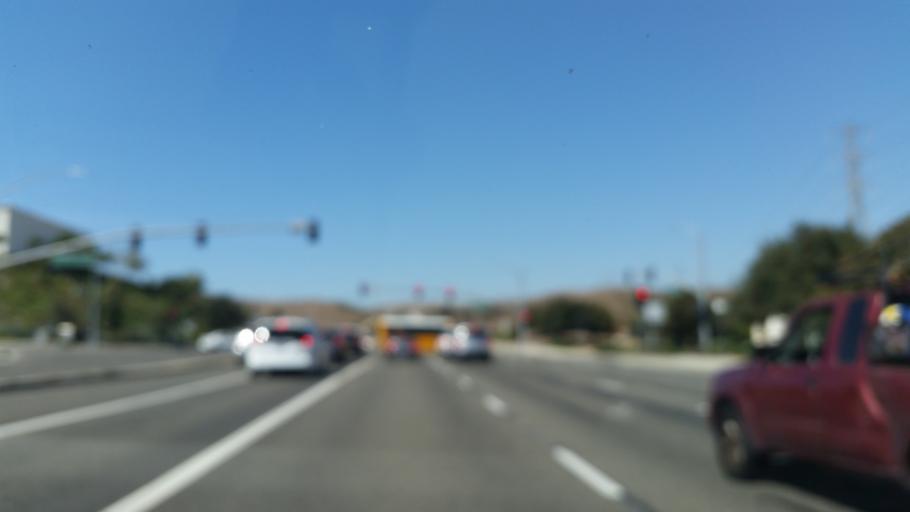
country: US
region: California
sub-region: Orange County
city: San Clemente
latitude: 33.4634
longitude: -117.6042
